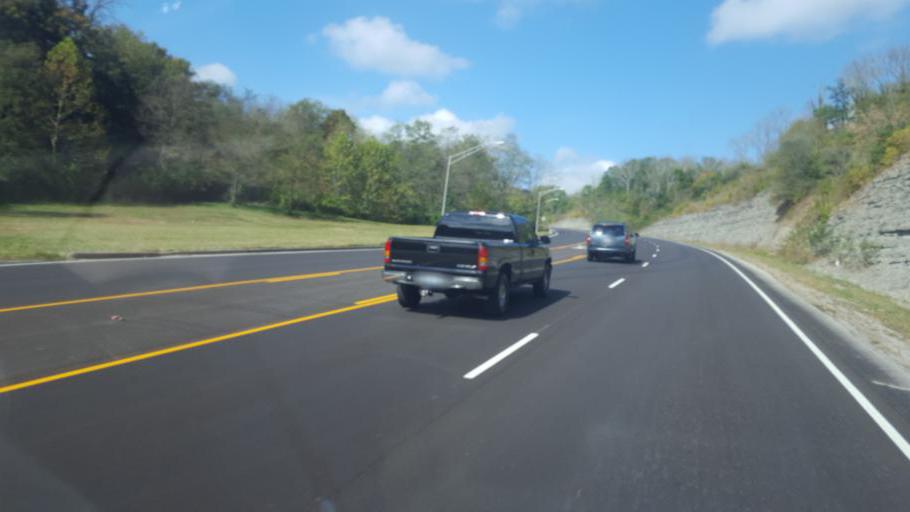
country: US
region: Ohio
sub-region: Brown County
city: Aberdeen
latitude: 38.6419
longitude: -83.7707
